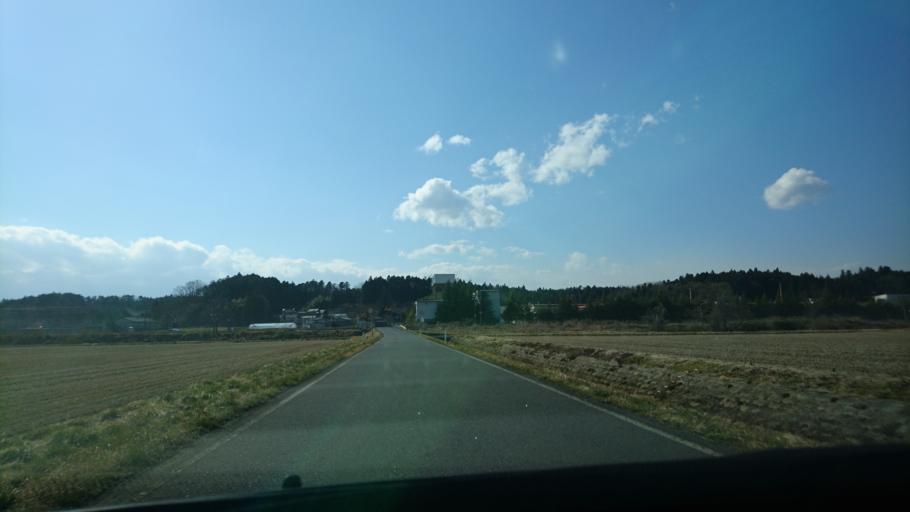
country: JP
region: Iwate
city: Ichinoseki
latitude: 38.7936
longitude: 141.1763
